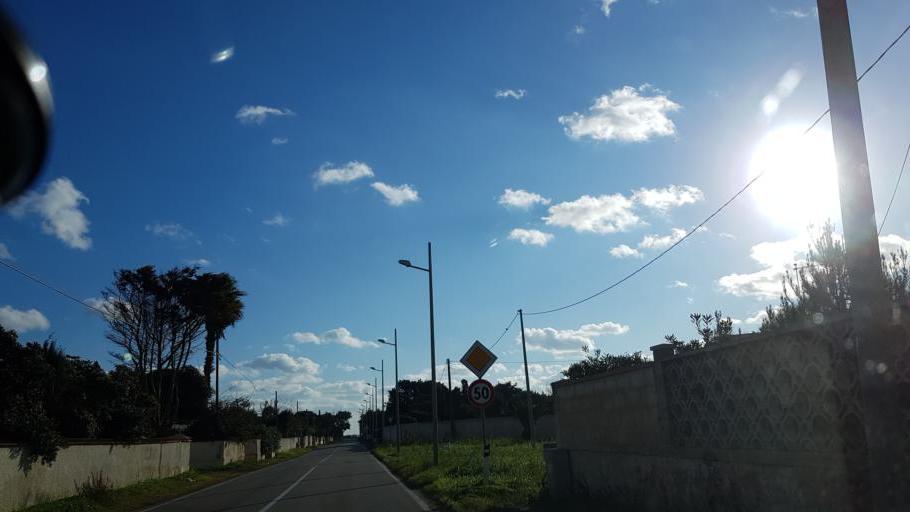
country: IT
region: Apulia
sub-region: Provincia di Brindisi
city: Materdomini
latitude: 40.6792
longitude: 17.9345
